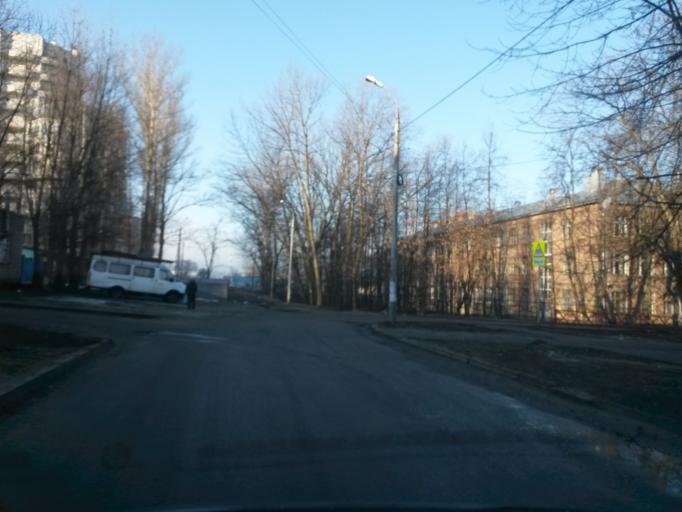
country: RU
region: Jaroslavl
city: Yaroslavl
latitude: 57.5788
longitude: 39.8439
